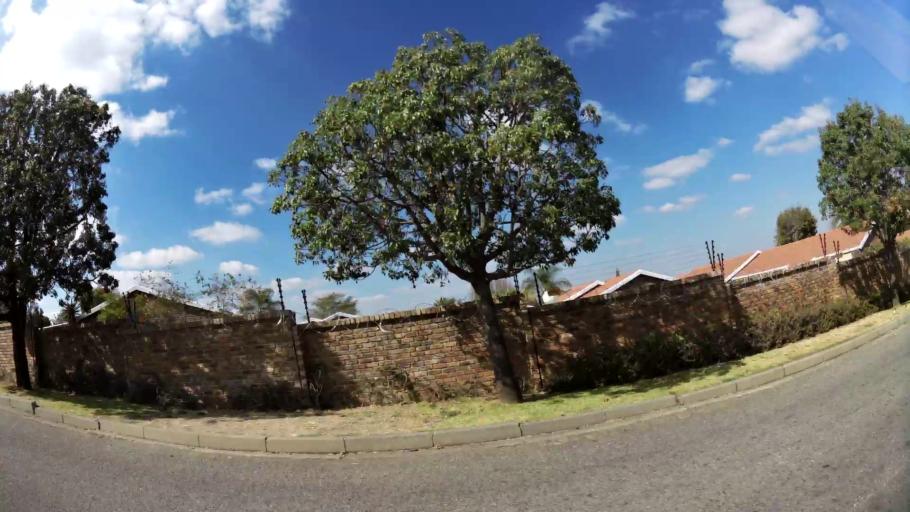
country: ZA
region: Gauteng
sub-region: West Rand District Municipality
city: Muldersdriseloop
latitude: -26.0658
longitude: 27.9590
